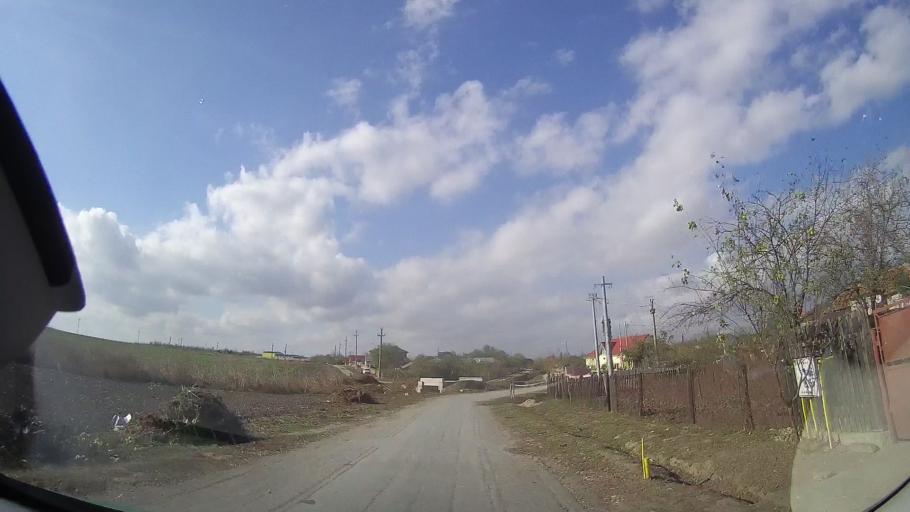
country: RO
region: Constanta
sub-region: Comuna Douazeci si Trei August
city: Douazeci si Trei August
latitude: 43.9125
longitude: 28.5873
